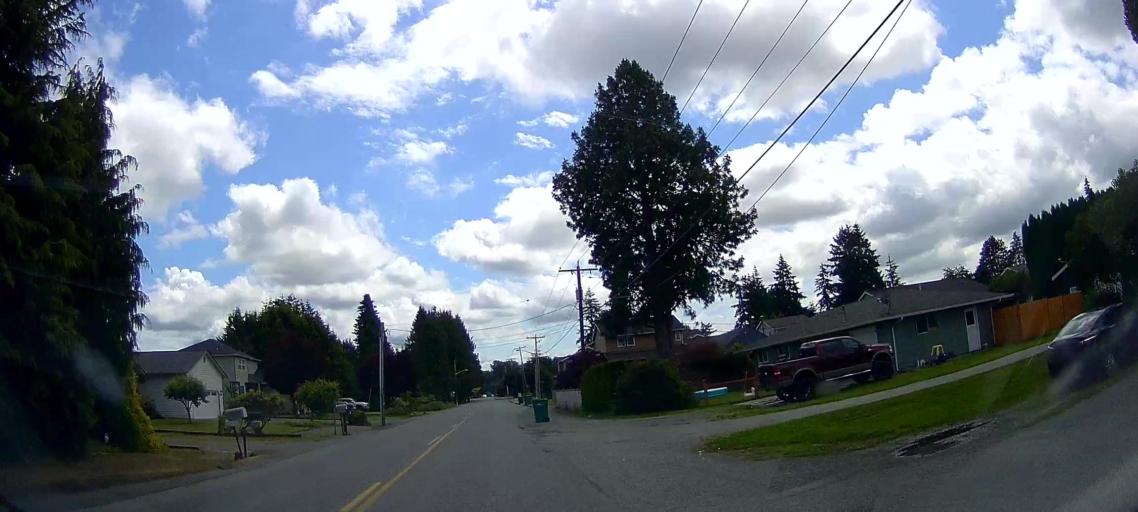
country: US
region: Washington
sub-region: Skagit County
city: Burlington
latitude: 48.4768
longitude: -122.3085
